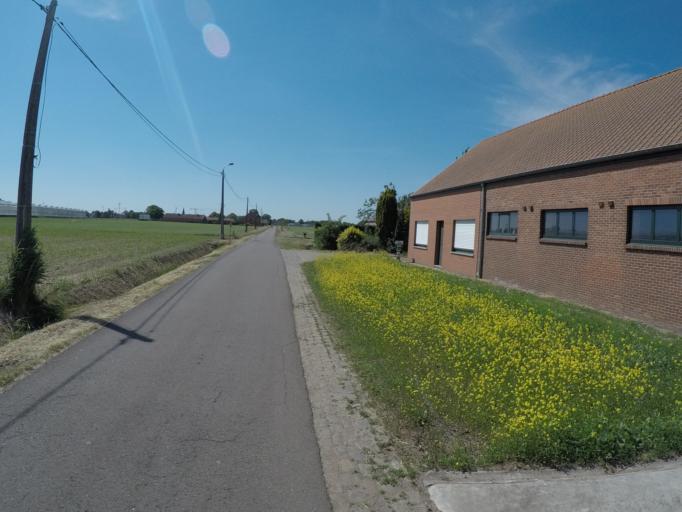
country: BE
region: Flanders
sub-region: Provincie Antwerpen
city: Wuustwezel
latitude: 51.4101
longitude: 4.6397
